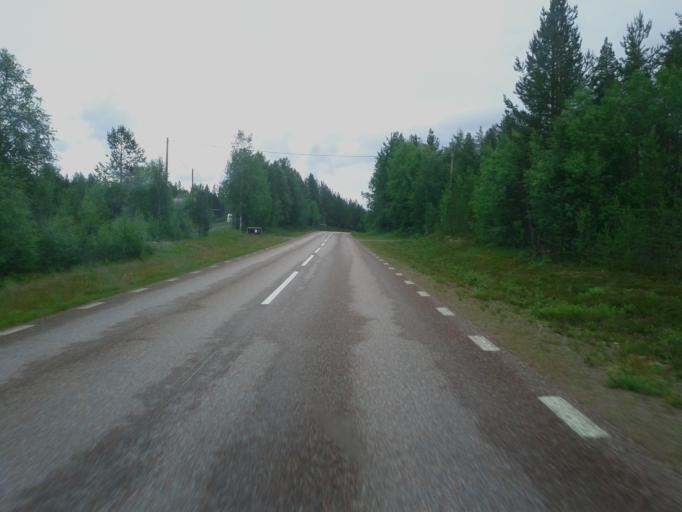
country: NO
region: Hedmark
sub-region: Trysil
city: Innbygda
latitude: 61.7236
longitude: 12.9959
